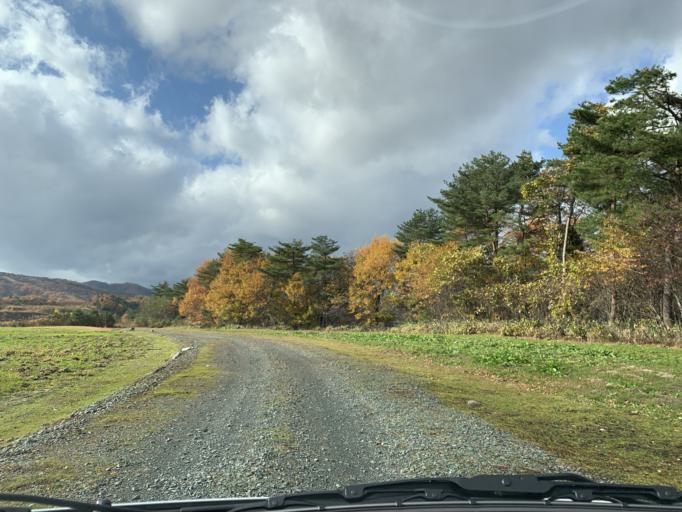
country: JP
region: Iwate
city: Mizusawa
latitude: 39.1131
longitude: 140.9536
